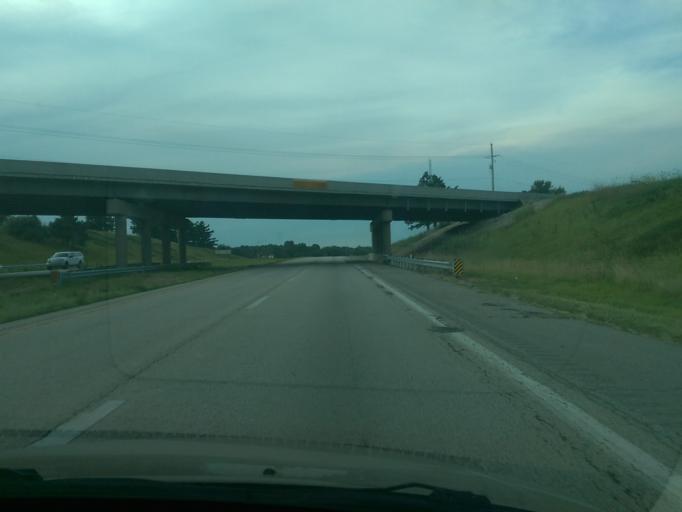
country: US
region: Missouri
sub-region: Andrew County
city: Country Club Village
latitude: 39.8145
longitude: -94.8033
